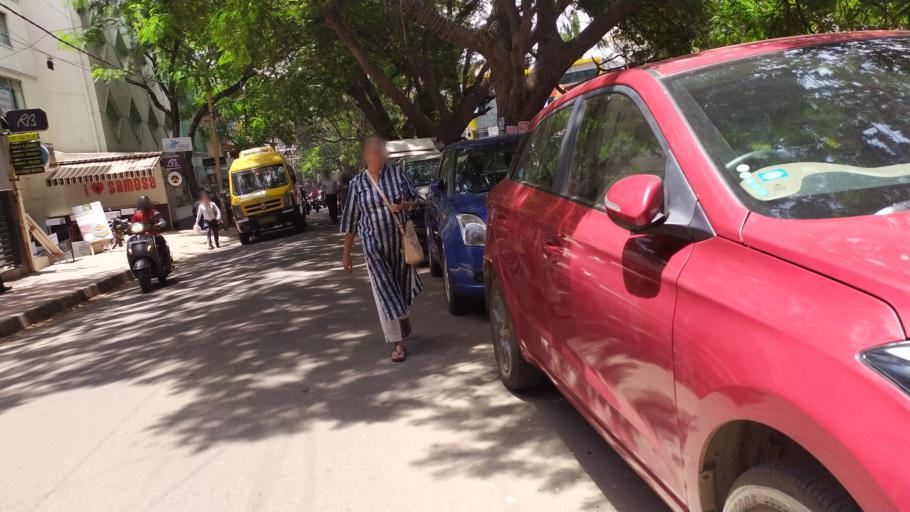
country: IN
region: Karnataka
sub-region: Bangalore Urban
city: Bangalore
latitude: 12.9331
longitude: 77.6149
